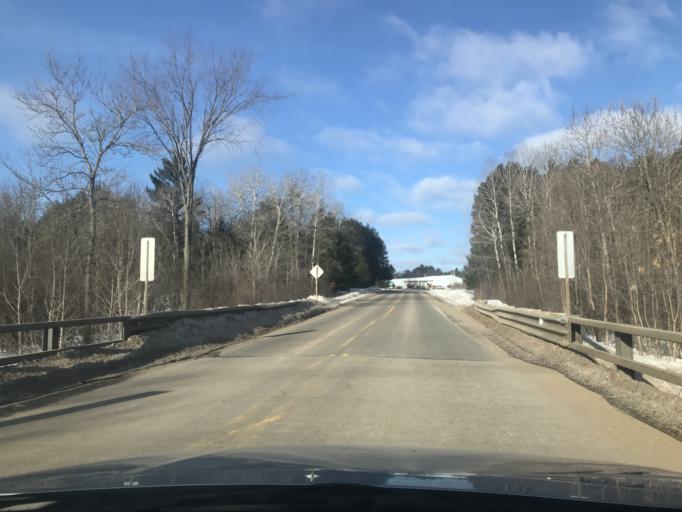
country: US
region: Wisconsin
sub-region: Marinette County
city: Niagara
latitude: 45.6387
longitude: -87.9769
